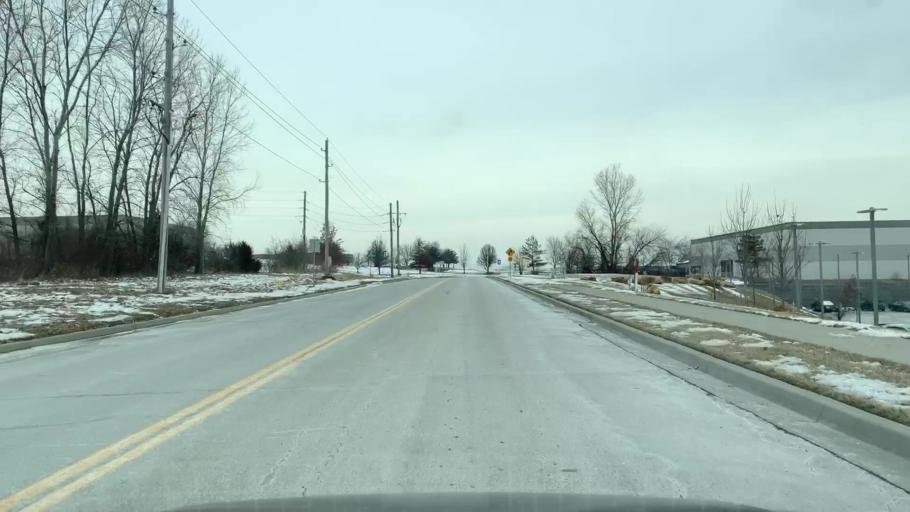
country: US
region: Missouri
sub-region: Jackson County
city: Lees Summit
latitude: 38.9525
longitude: -94.3639
